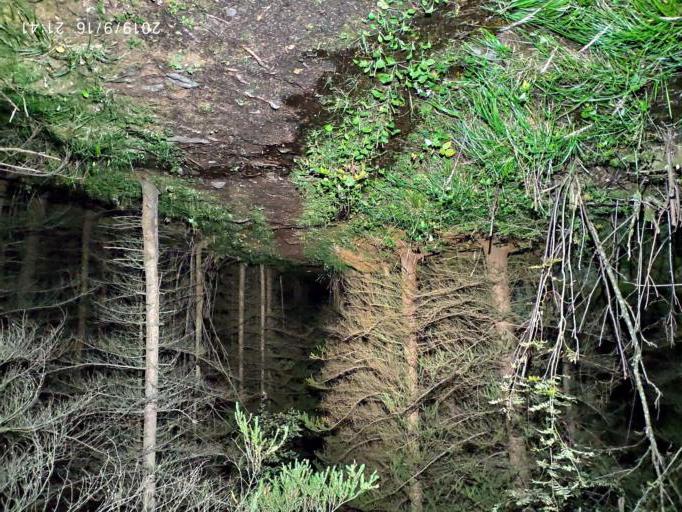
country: NO
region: Oppland
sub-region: Oyer
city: Tretten
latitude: 61.3074
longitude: 10.2822
